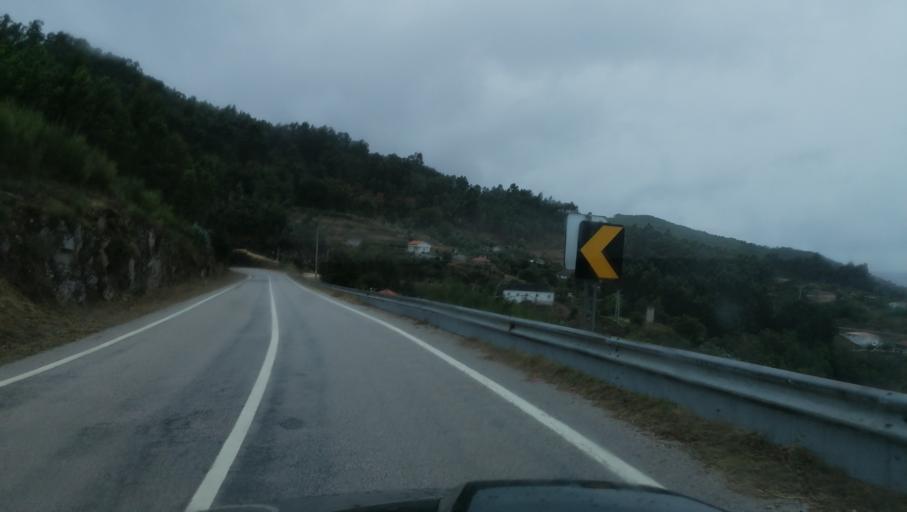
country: PT
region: Vila Real
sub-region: Ribeira de Pena
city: Sobreira
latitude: 41.5232
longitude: -7.8304
